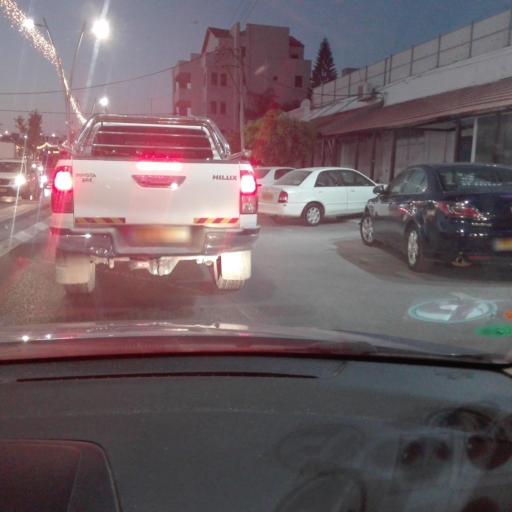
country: PS
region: West Bank
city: Nazlat `Isa
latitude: 32.4165
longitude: 35.0461
